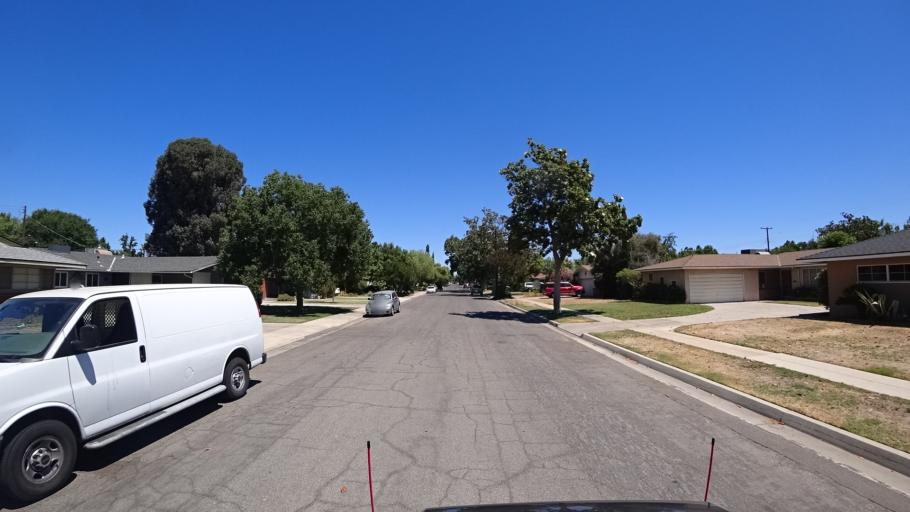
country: US
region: California
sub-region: Fresno County
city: Fresno
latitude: 36.7743
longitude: -119.8143
